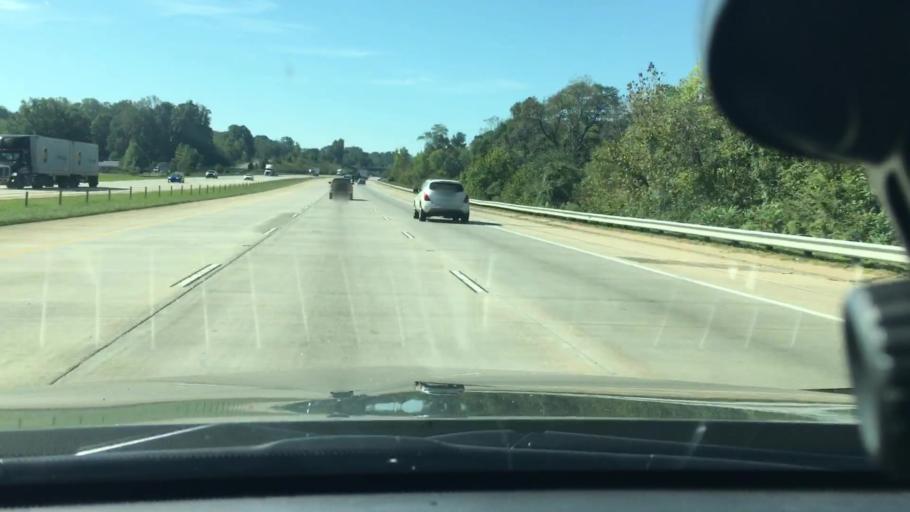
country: US
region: North Carolina
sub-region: Gaston County
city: Mount Holly
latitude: 35.3032
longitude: -80.9554
